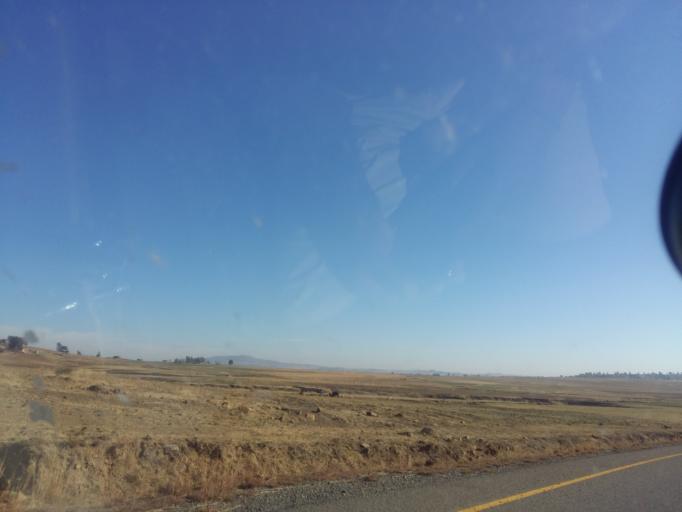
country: LS
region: Mafeteng
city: Mafeteng
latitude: -29.6798
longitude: 27.2779
